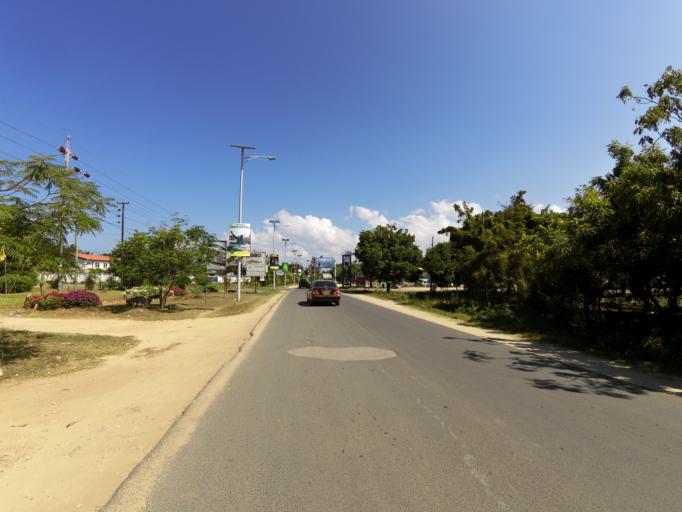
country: TZ
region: Dar es Salaam
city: Magomeni
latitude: -6.7491
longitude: 39.2843
